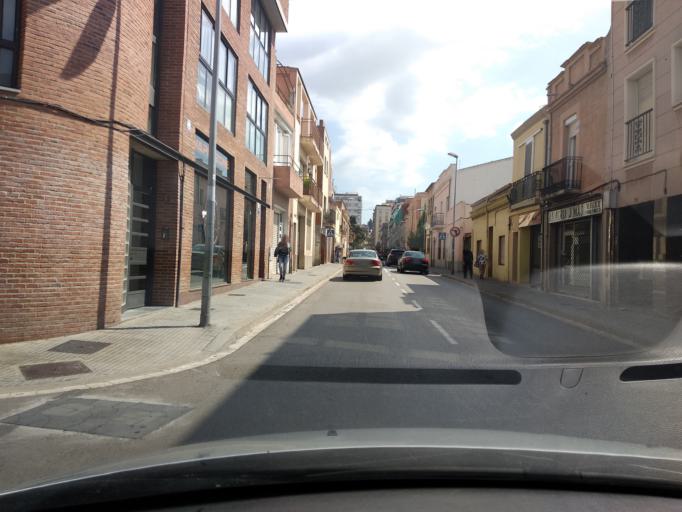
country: ES
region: Catalonia
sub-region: Provincia de Barcelona
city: Granollers
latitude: 41.6106
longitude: 2.2871
